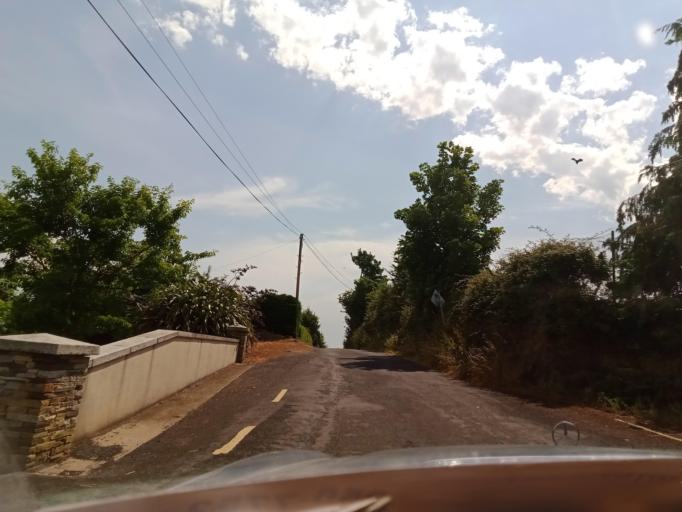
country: IE
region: Leinster
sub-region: Kilkenny
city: Mooncoin
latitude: 52.2707
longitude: -7.2151
